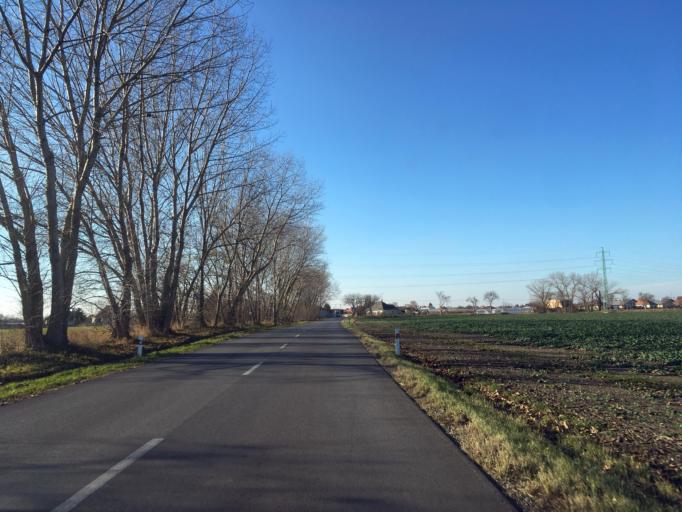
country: SK
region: Nitriansky
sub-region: Okres Komarno
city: Hurbanovo
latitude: 47.8990
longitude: 18.1571
